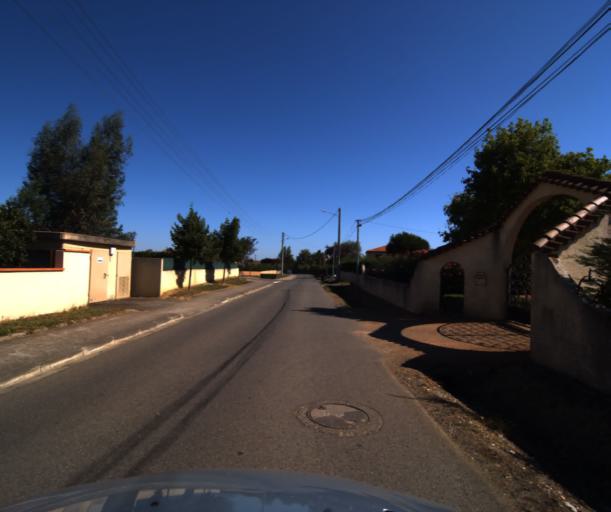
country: FR
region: Midi-Pyrenees
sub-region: Departement de la Haute-Garonne
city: Eaunes
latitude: 43.4239
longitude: 1.3483
